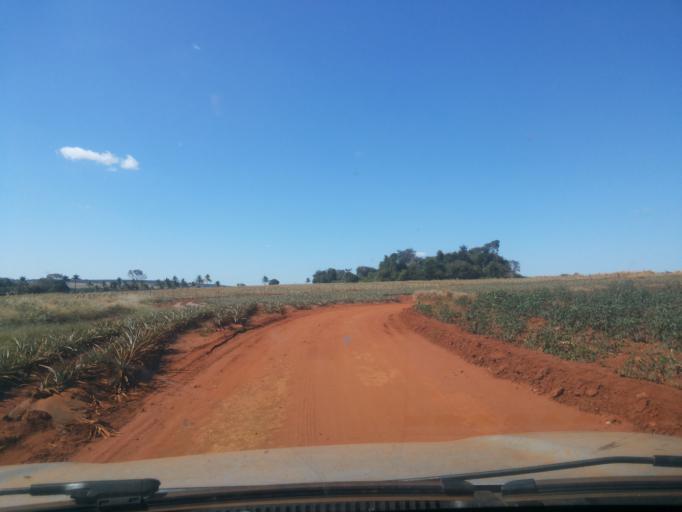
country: BR
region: Minas Gerais
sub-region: Centralina
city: Centralina
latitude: -18.7397
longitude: -49.1933
